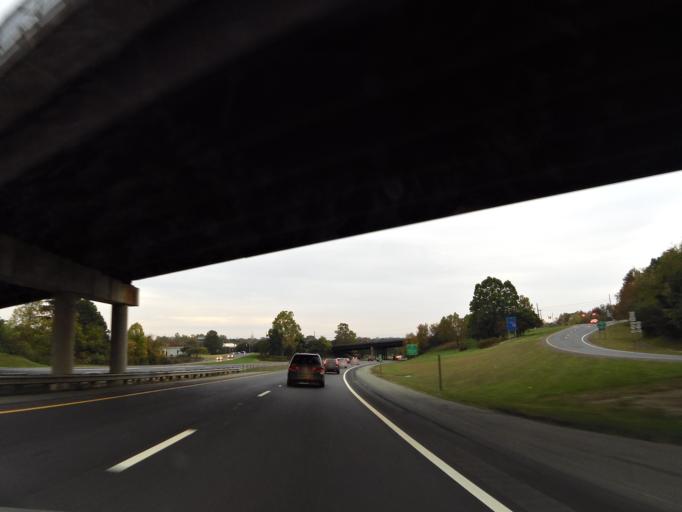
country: US
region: North Carolina
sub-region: Catawba County
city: Hickory
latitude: 35.7245
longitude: -81.3574
